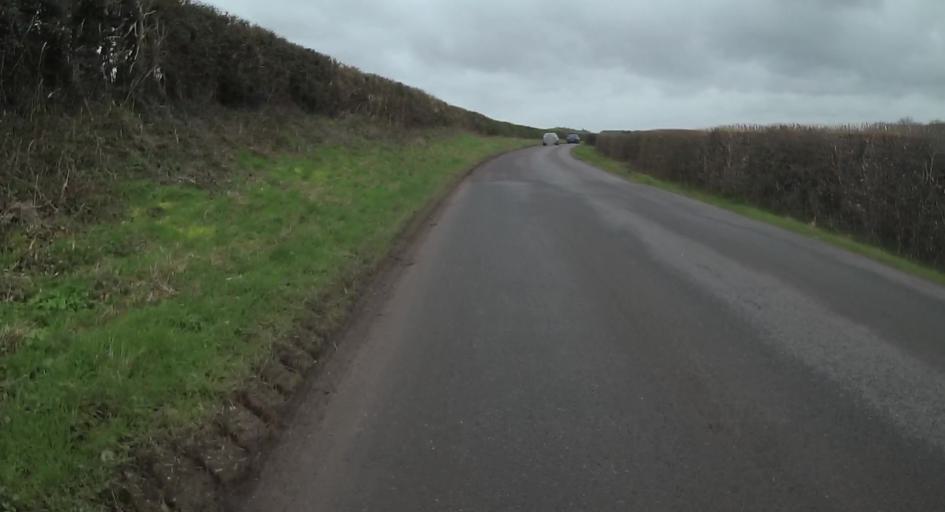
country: GB
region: England
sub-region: Hampshire
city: Kingsclere
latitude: 51.3280
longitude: -1.2710
